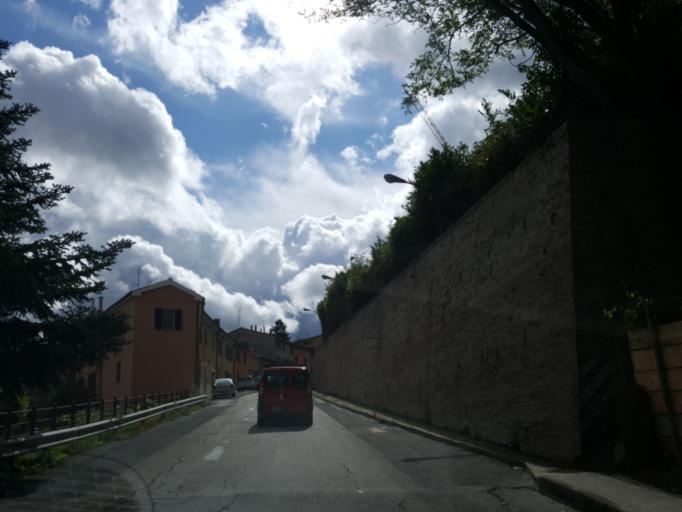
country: IT
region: The Marches
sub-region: Provincia di Macerata
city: Camerino
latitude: 43.1404
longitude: 13.0746
